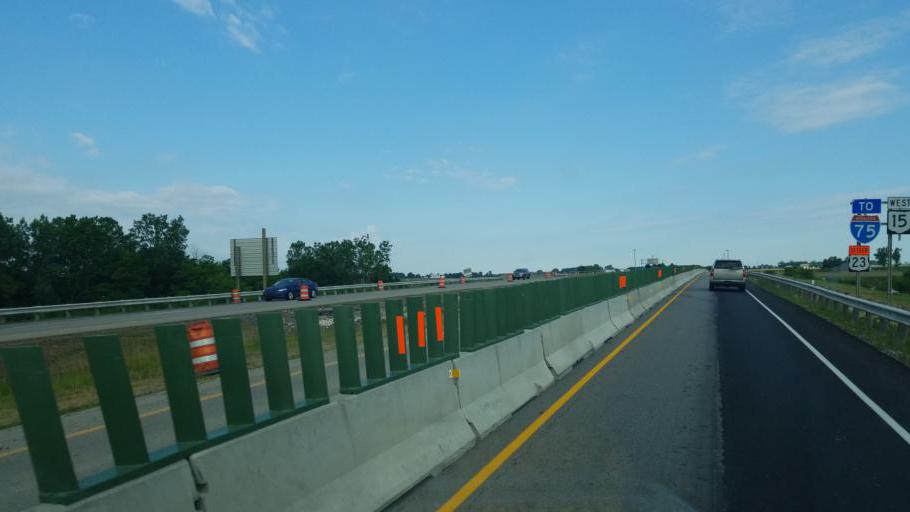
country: US
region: Ohio
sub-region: Wyandot County
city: Carey
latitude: 40.9447
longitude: -83.4096
